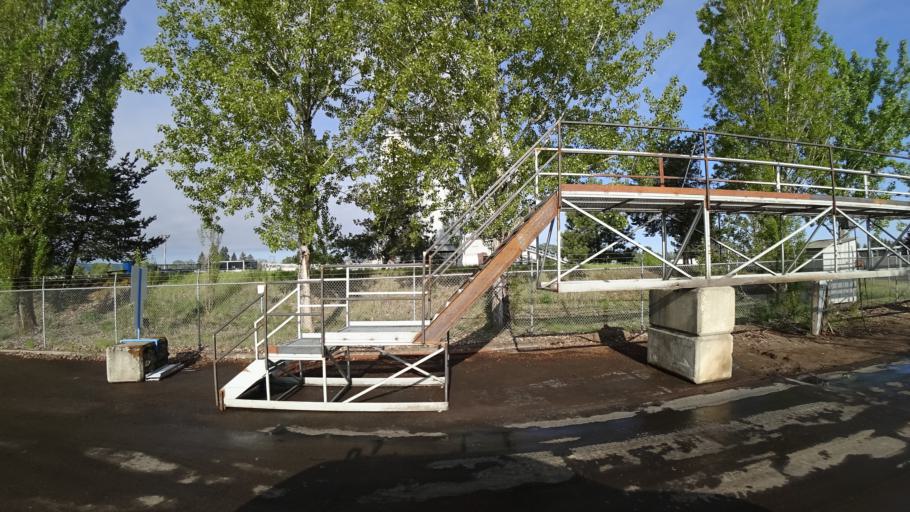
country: US
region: Oregon
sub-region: Washington County
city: Hillsboro
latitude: 45.5132
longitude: -123.0013
